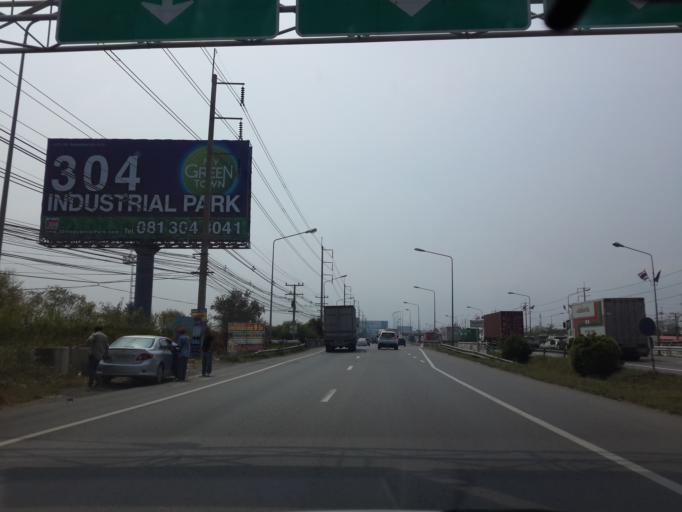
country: TH
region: Chon Buri
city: Chon Buri
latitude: 13.4381
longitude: 101.0013
